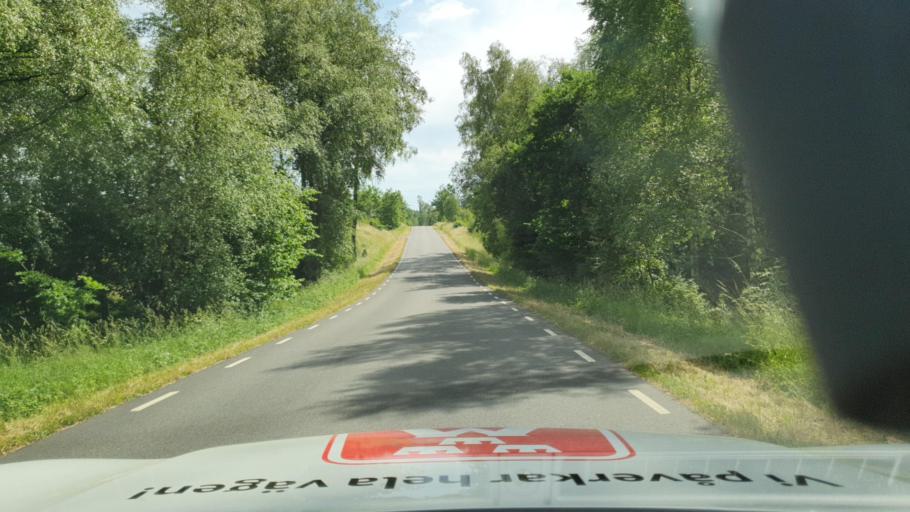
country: SE
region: Skane
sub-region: Tomelilla Kommun
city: Tomelilla
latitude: 55.6963
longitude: 13.9531
